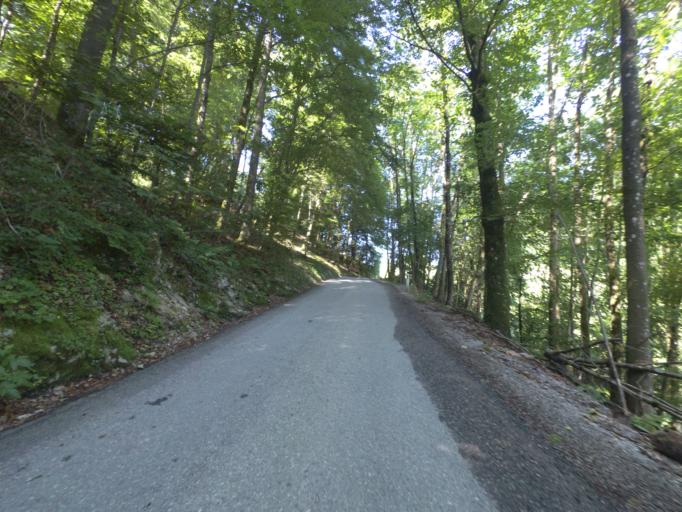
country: AT
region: Salzburg
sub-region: Politischer Bezirk Salzburg-Umgebung
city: Elsbethen
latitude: 47.7584
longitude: 13.1036
